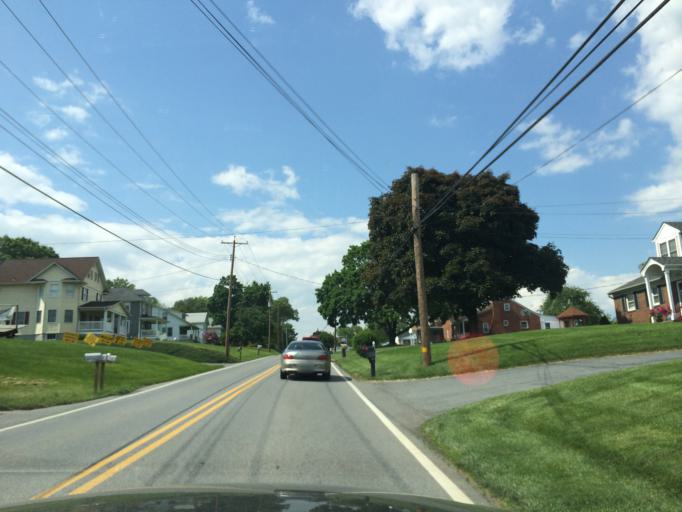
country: US
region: Maryland
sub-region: Carroll County
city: Sykesville
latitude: 39.3713
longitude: -77.0563
